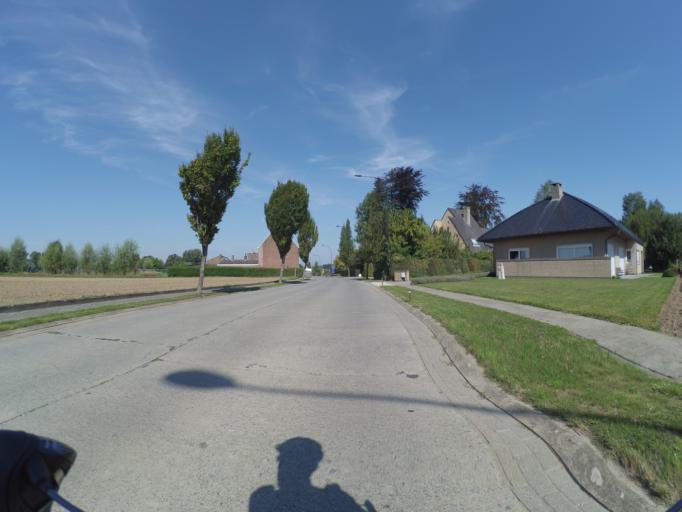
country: BE
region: Flanders
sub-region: Provincie Oost-Vlaanderen
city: Oudenaarde
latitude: 50.8153
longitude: 3.6244
